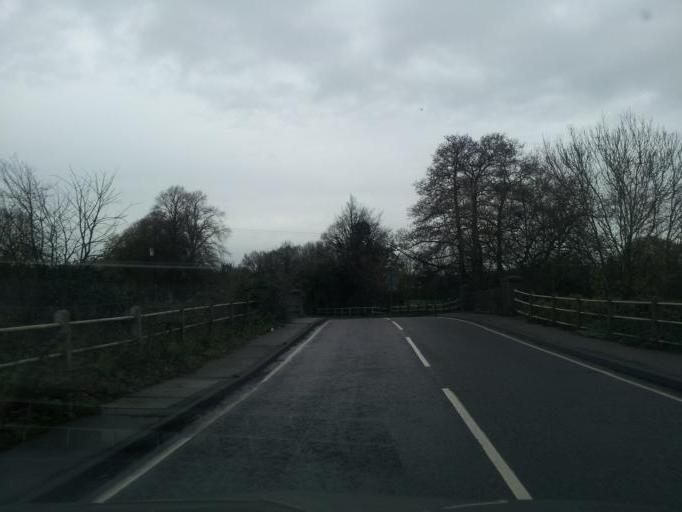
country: GB
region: England
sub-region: Essex
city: Earls Colne
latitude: 51.9367
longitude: 0.6549
